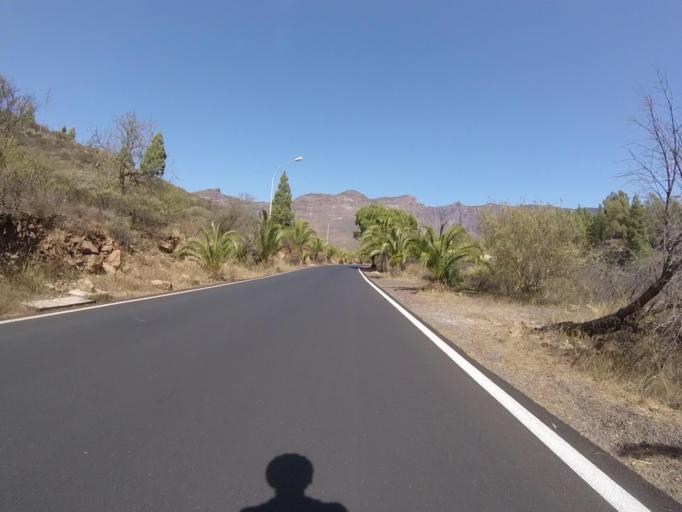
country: ES
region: Canary Islands
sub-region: Provincia de Las Palmas
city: San Bartolome
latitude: 27.9182
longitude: -15.5752
